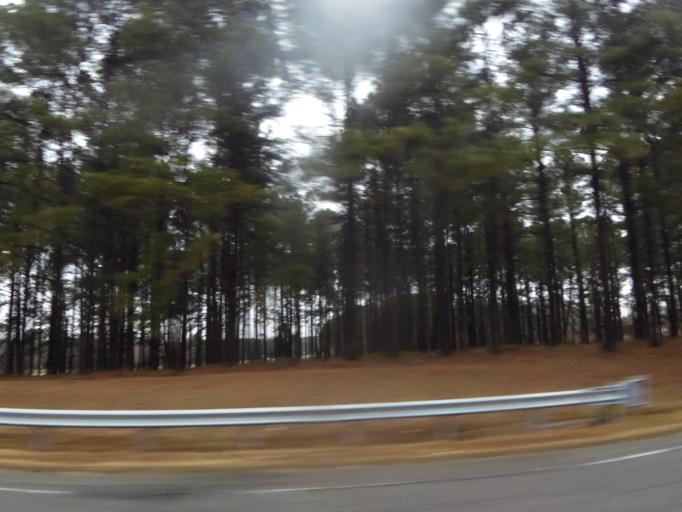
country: US
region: North Carolina
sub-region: Nash County
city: Red Oak
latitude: 35.9820
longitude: -77.8754
